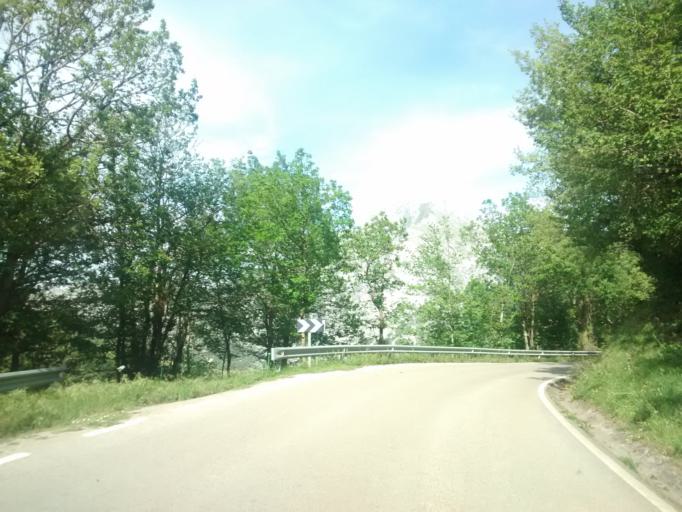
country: ES
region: Cantabria
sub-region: Provincia de Cantabria
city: Potes
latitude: 43.1905
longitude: -4.6195
